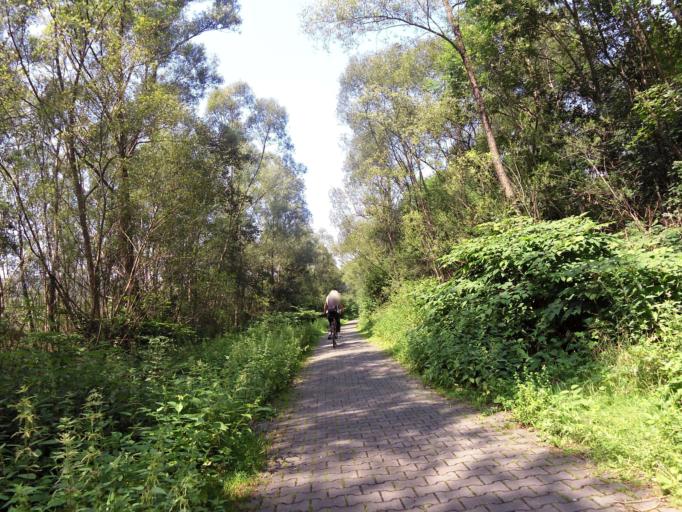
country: PL
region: Silesian Voivodeship
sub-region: Powiat zywiecki
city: Milowka
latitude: 49.5487
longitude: 19.0940
